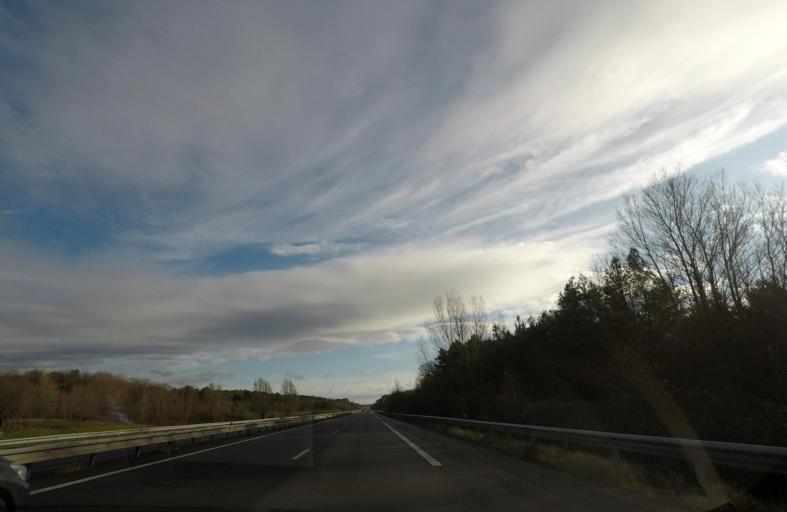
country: FR
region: Centre
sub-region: Departement du Loir-et-Cher
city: Villefranche-sur-Cher
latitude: 47.3159
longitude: 1.8063
